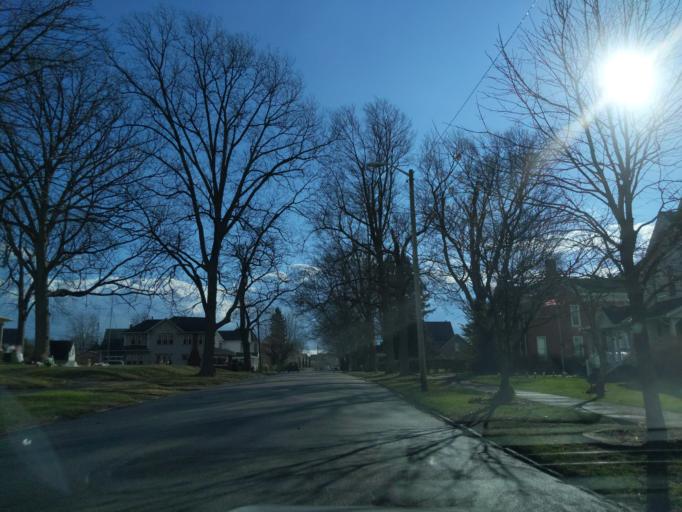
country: US
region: Indiana
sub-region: Decatur County
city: Greensburg
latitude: 39.3408
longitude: -85.4878
